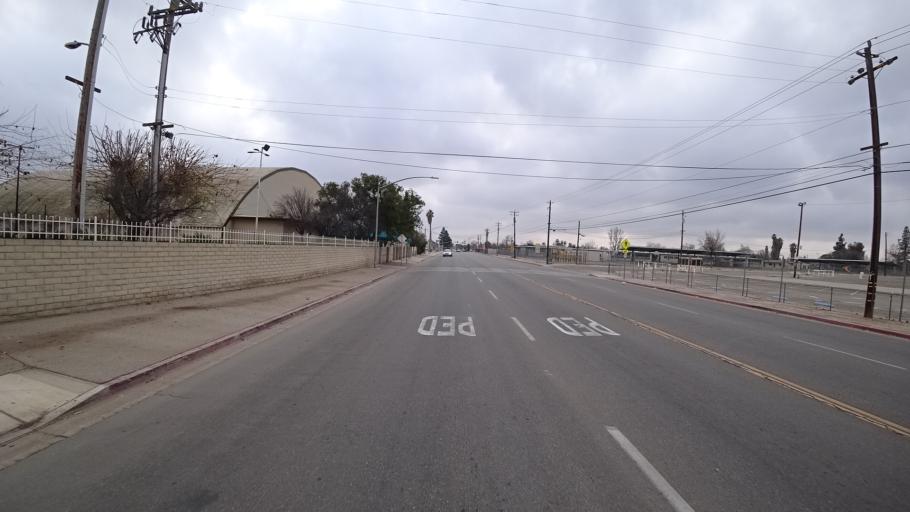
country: US
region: California
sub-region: Kern County
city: Bakersfield
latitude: 35.3418
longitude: -119.0118
